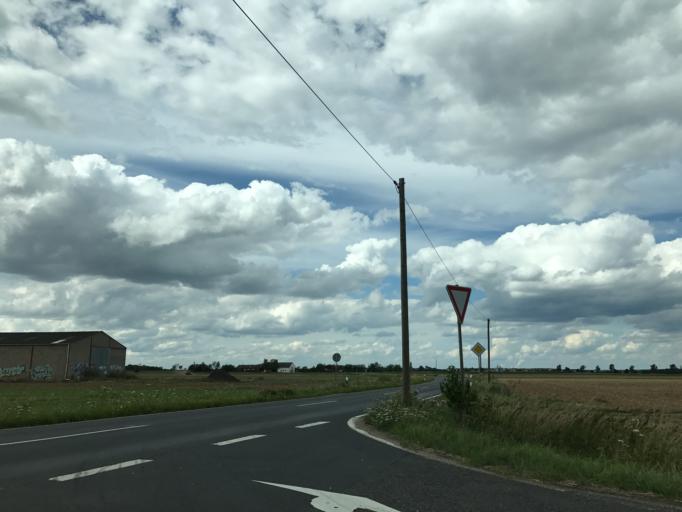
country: DE
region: North Rhine-Westphalia
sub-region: Regierungsbezirk Koln
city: Rheinbach
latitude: 50.6735
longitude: 6.9109
